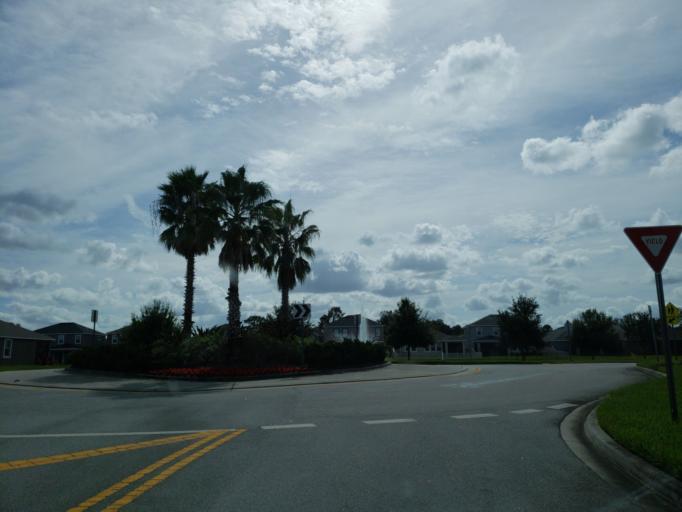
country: US
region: Florida
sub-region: Hillsborough County
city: Riverview
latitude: 27.8534
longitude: -82.3338
